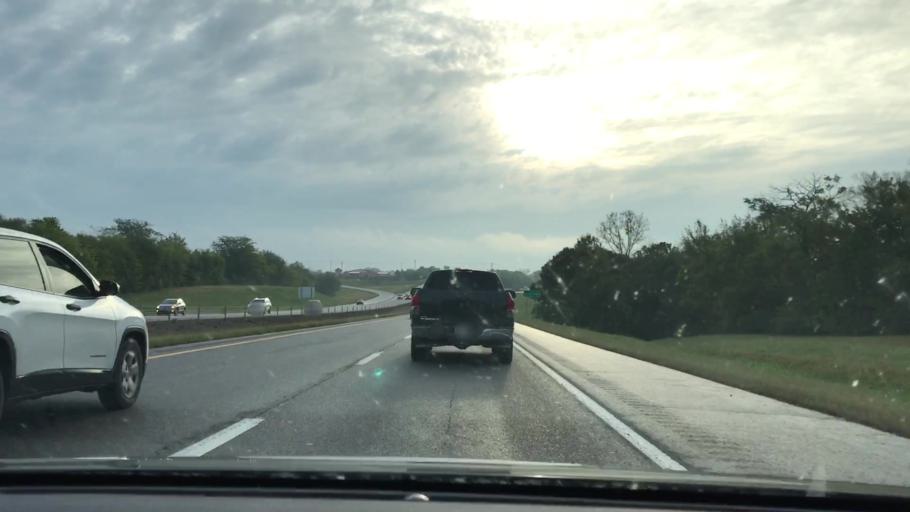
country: US
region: Tennessee
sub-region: Sumner County
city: Hendersonville
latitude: 36.3303
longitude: -86.5719
